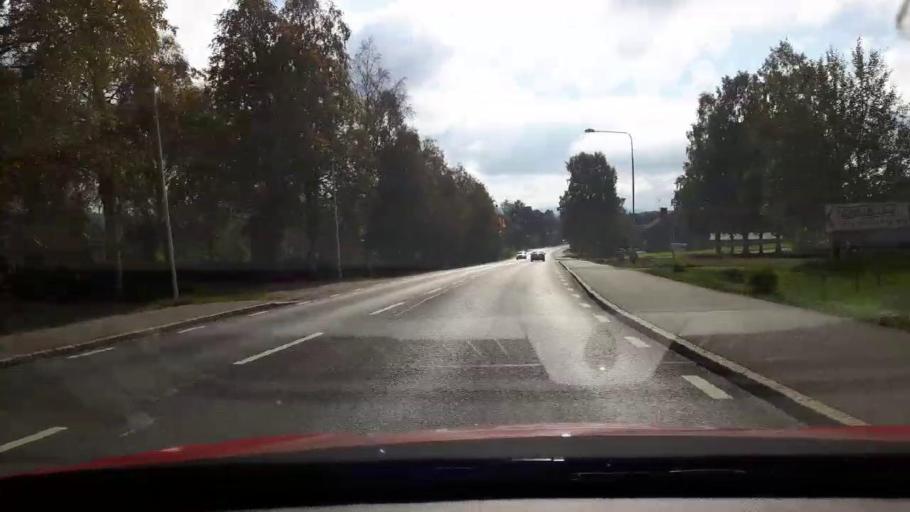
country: SE
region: Gaevleborg
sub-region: Ljusdals Kommun
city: Jaervsoe
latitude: 61.7205
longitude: 16.1686
